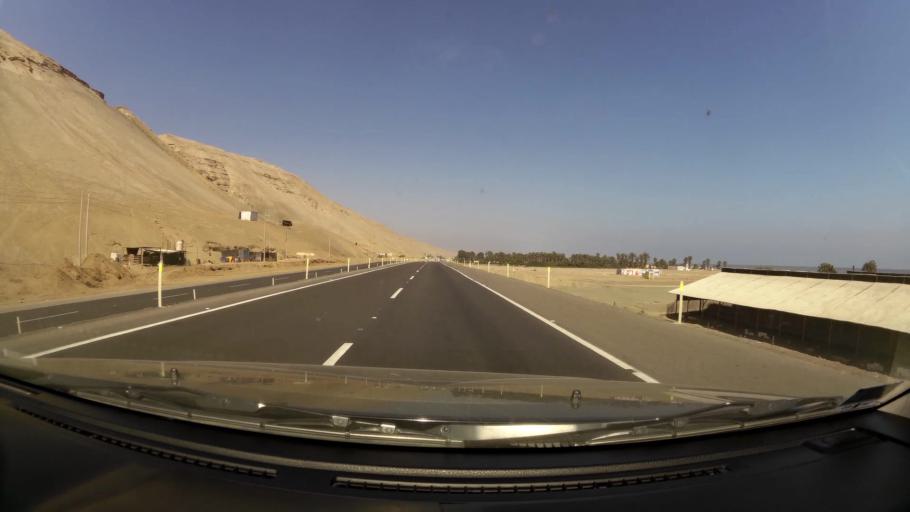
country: PE
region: Ica
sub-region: Provincia de Chincha
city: San Pedro
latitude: -13.3590
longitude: -76.2181
